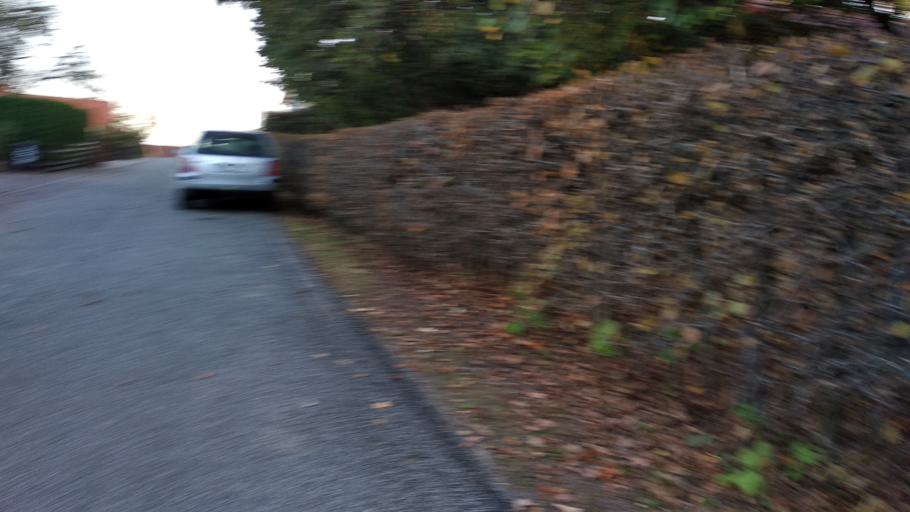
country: DE
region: Bavaria
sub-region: Upper Bavaria
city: Glonn
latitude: 47.9700
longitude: 11.8352
